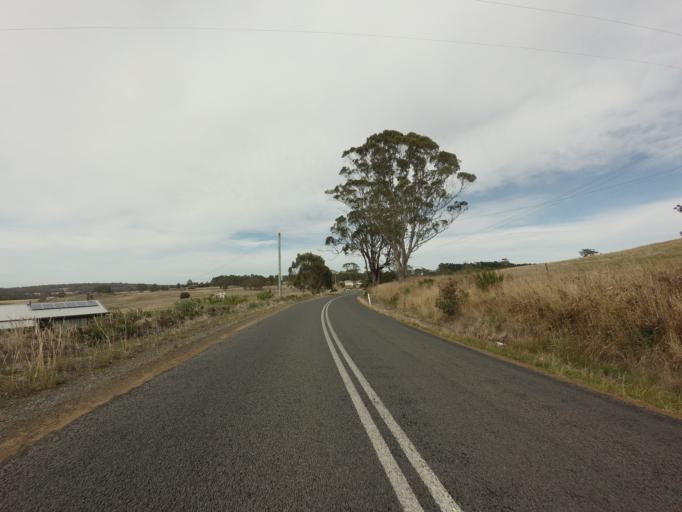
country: AU
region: Tasmania
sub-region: Brighton
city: Bridgewater
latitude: -42.3826
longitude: 147.4242
